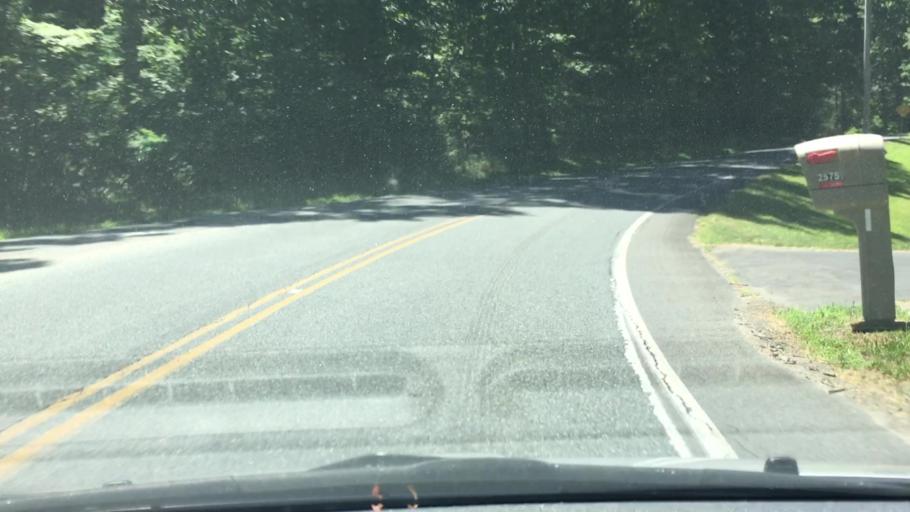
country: US
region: Maryland
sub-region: Saint Mary's County
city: California
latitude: 38.3751
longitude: -76.5770
